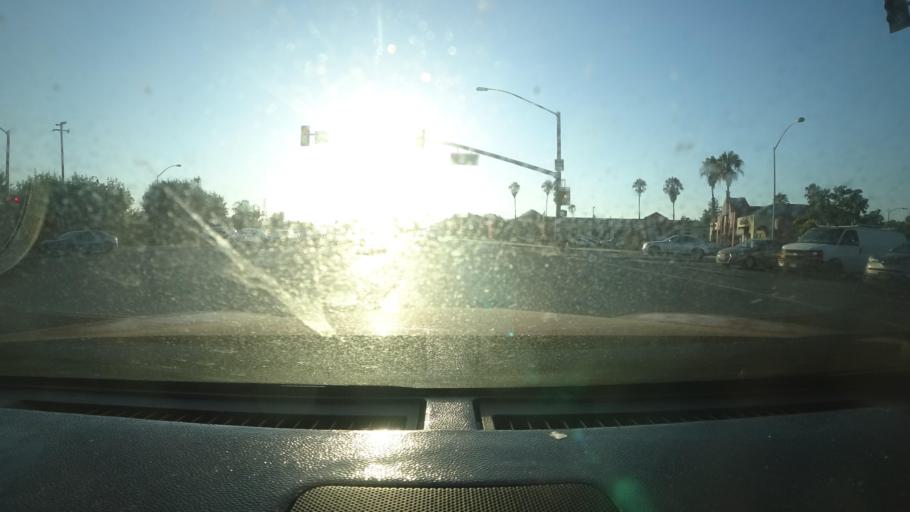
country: US
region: California
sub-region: Santa Clara County
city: Alum Rock
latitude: 37.3554
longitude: -121.8305
